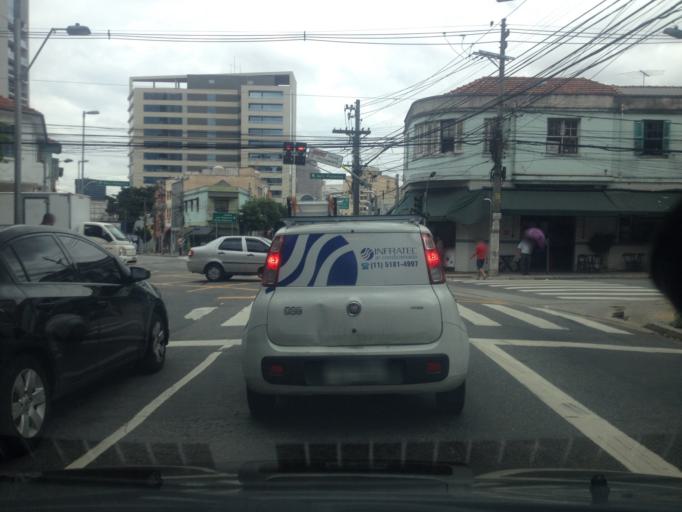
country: BR
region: Sao Paulo
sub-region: Sao Paulo
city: Sao Paulo
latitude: -23.5640
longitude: -46.6924
